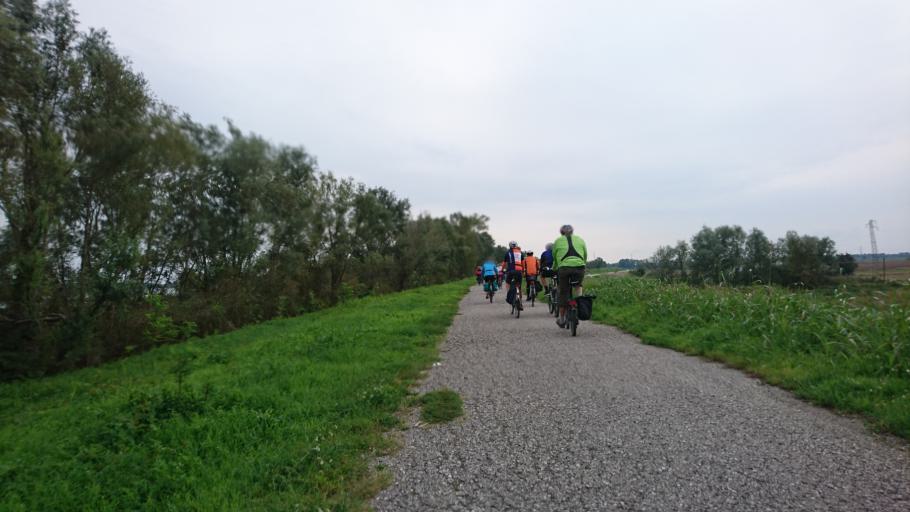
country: IT
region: Veneto
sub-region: Provincia di Rovigo
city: Scardovari
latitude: 44.9546
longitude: 12.4166
